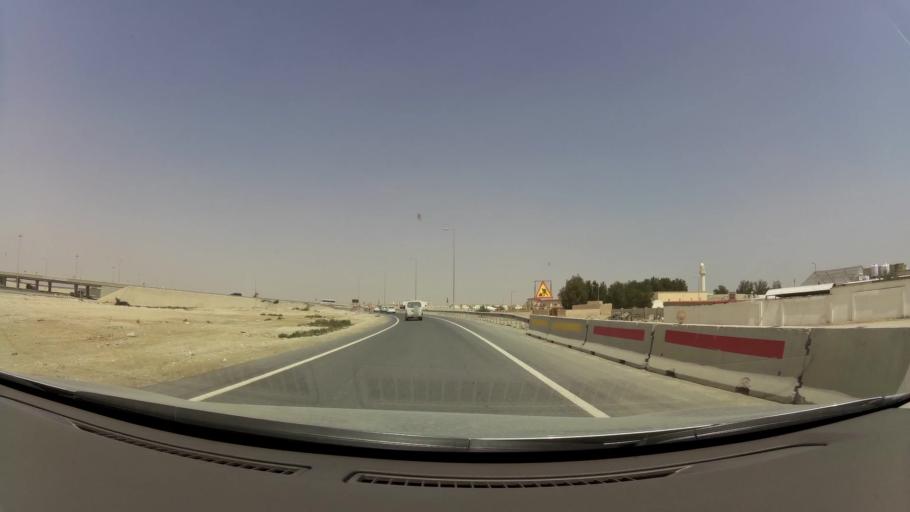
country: QA
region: Baladiyat Umm Salal
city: Umm Salal `Ali
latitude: 25.4842
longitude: 51.4085
